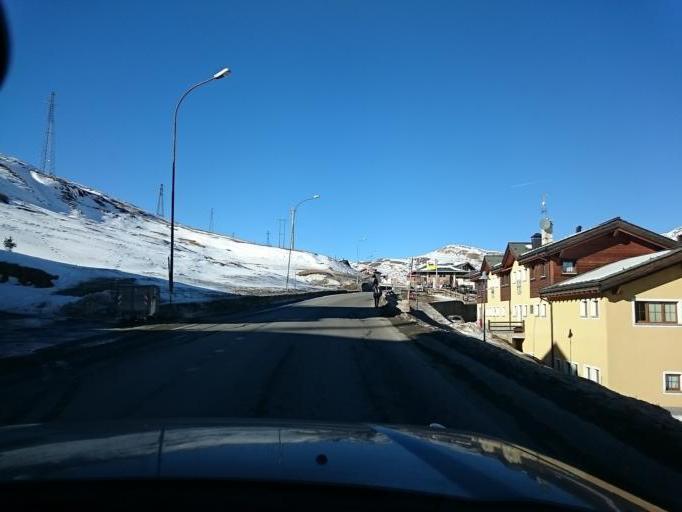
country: IT
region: Lombardy
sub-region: Provincia di Sondrio
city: Livigno
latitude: 46.5252
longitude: 10.1762
